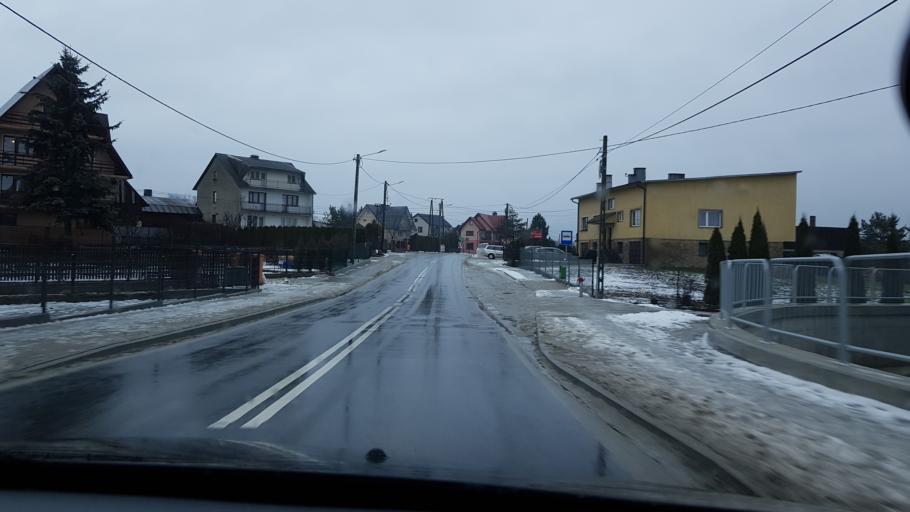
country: PL
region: Lesser Poland Voivodeship
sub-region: Powiat nowotarski
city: Nowy Targ
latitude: 49.4839
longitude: 20.0050
